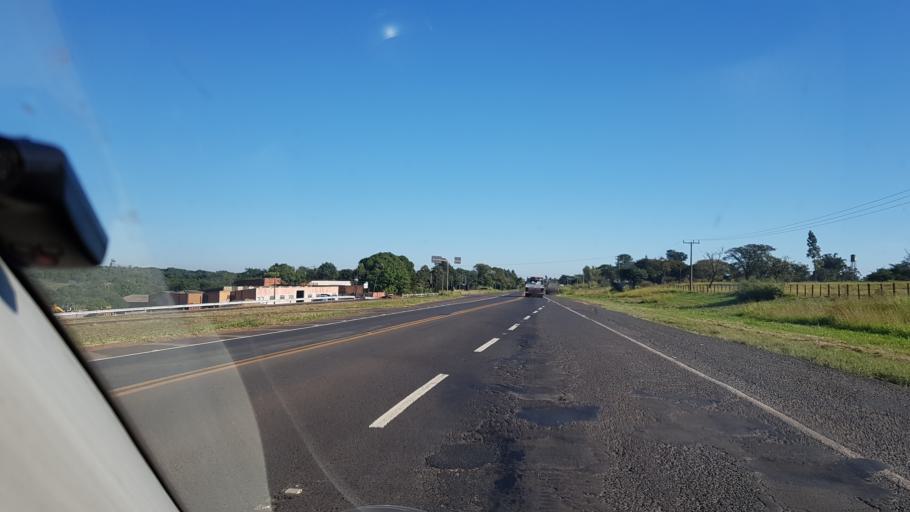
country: BR
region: Sao Paulo
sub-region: Assis
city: Assis
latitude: -22.6344
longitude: -50.4356
